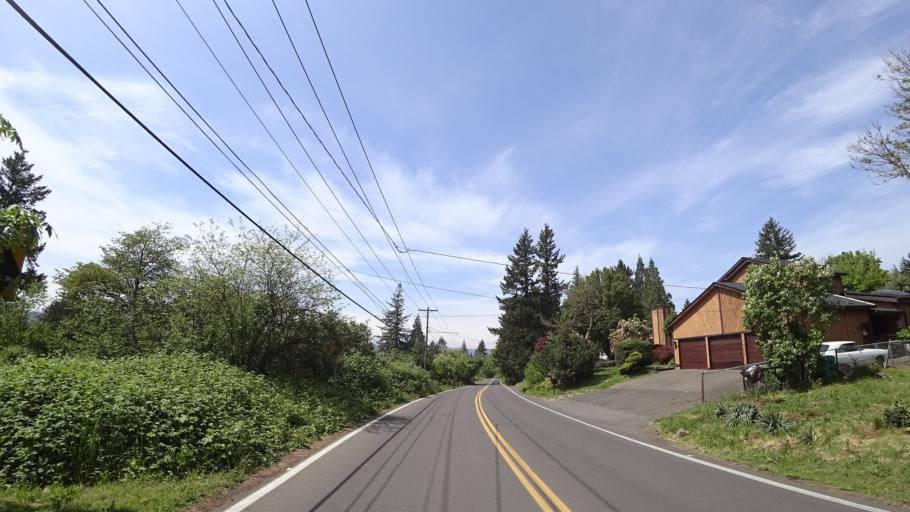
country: US
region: Oregon
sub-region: Clackamas County
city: Milwaukie
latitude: 45.4616
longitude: -122.6026
